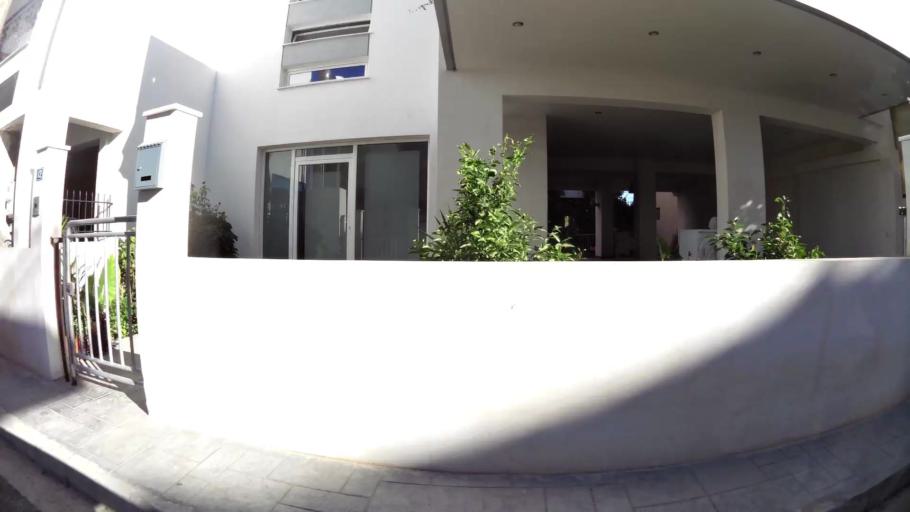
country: GR
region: Attica
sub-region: Nomarchia Anatolikis Attikis
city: Koropi
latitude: 37.9023
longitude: 23.8653
